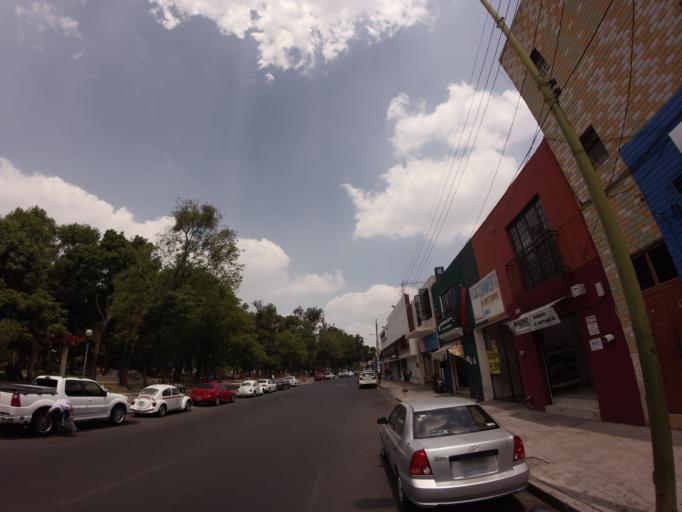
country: MX
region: Jalisco
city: Guadalajara
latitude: 20.6811
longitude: -103.3399
